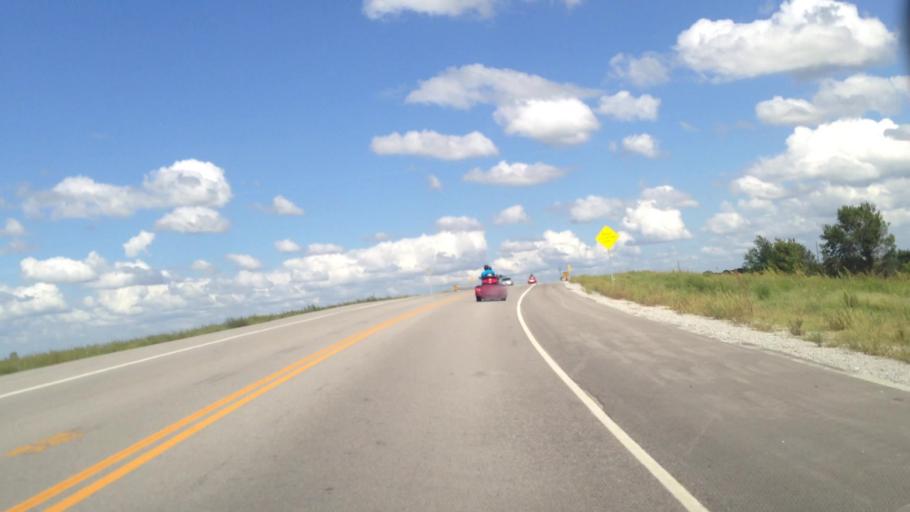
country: US
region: Kansas
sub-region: Labette County
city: Chetopa
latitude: 36.8897
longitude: -95.0963
